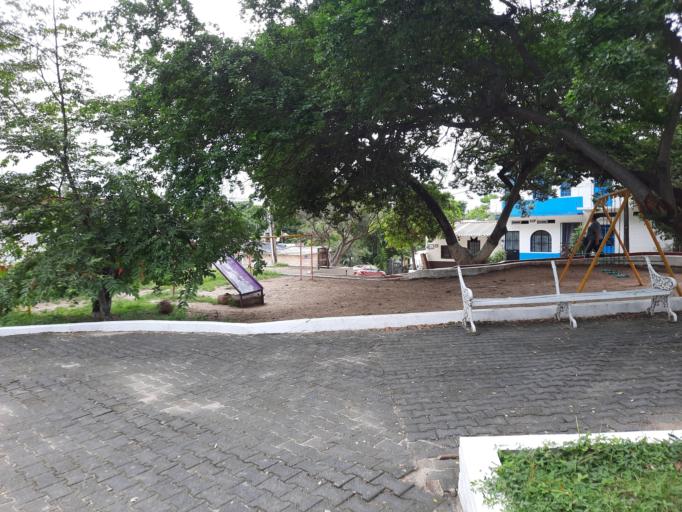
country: MX
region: Jalisco
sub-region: Puerto Vallarta
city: Puerto Vallarta
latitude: 20.6548
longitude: -105.2131
